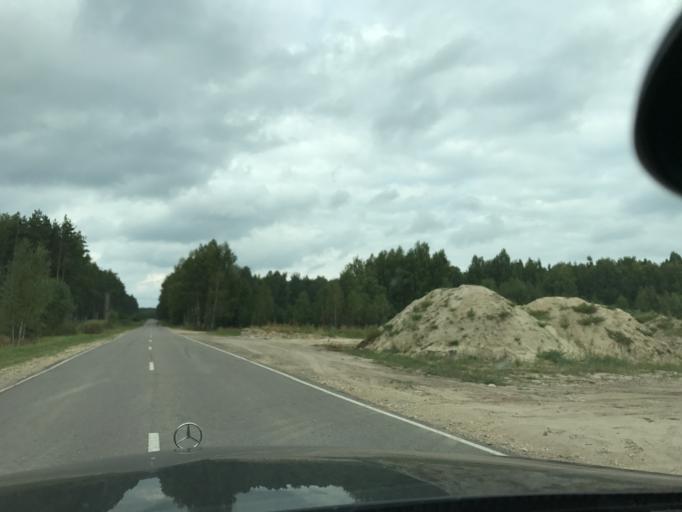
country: RU
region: Nizjnij Novgorod
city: Taremskoye
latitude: 56.0045
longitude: 42.9909
